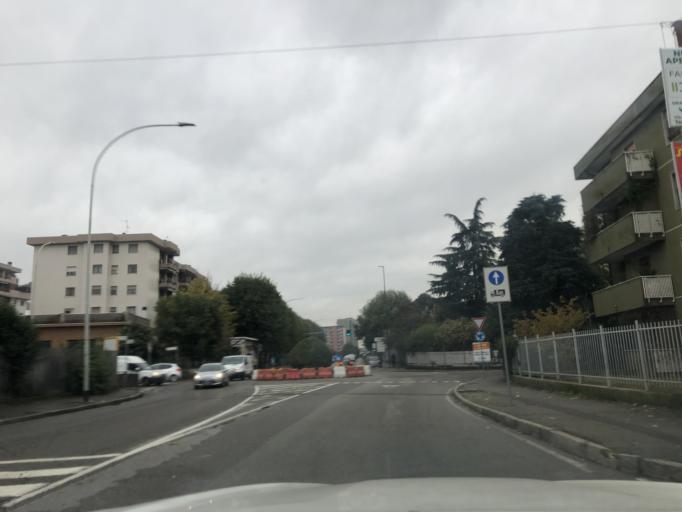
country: IT
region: Lombardy
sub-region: Citta metropolitana di Milano
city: Cesano Boscone
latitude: 45.4419
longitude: 9.1023
